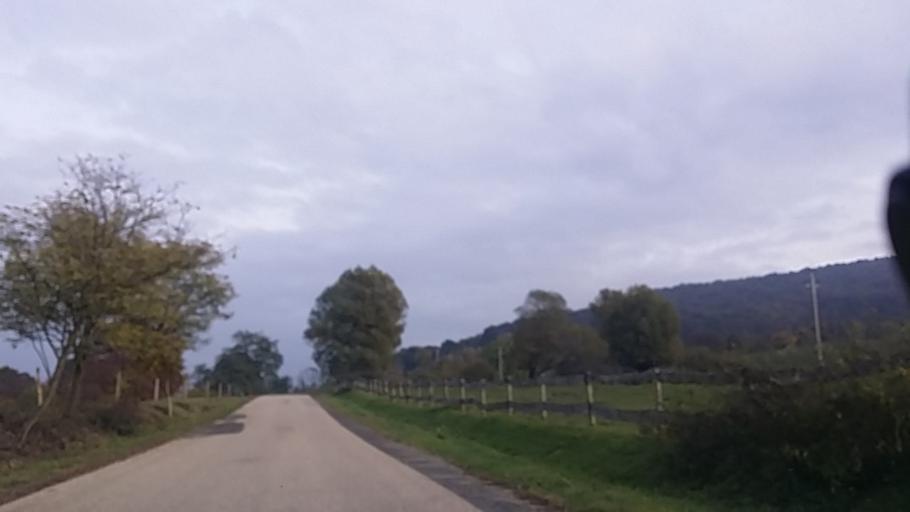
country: HU
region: Borsod-Abauj-Zemplen
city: Sajokaza
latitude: 48.2705
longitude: 20.5126
